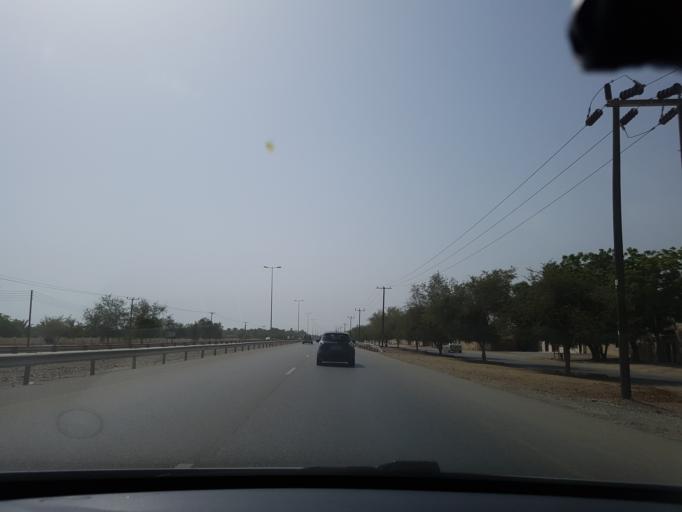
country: OM
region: Al Batinah
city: Al Khaburah
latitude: 23.9887
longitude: 57.0732
